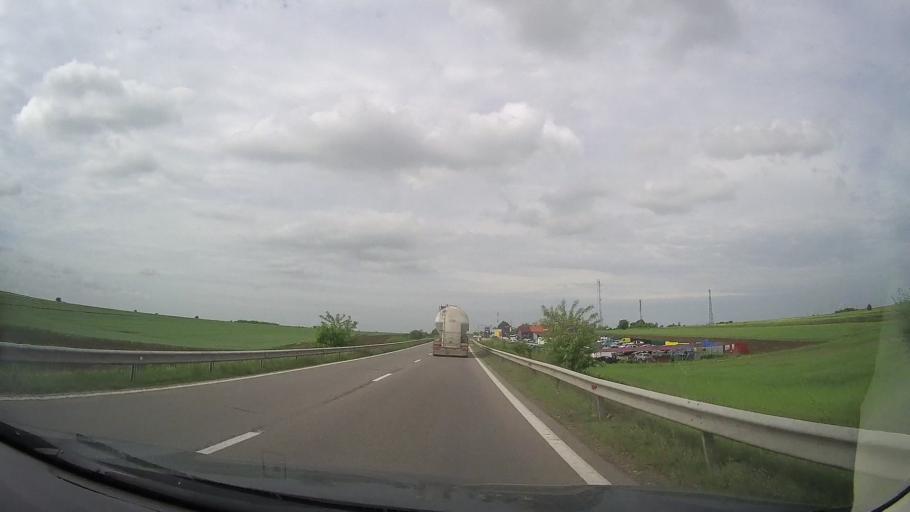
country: RO
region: Teleorman
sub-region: Comuna Vitanesti
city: Vitanesti
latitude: 44.0181
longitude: 25.4324
